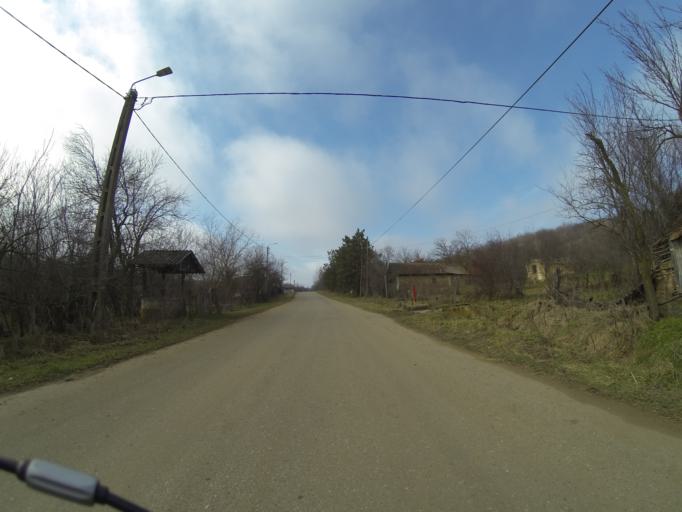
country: RO
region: Mehedinti
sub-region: Comuna Poroina Mare
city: Poroina Mare
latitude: 44.4944
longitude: 22.9949
